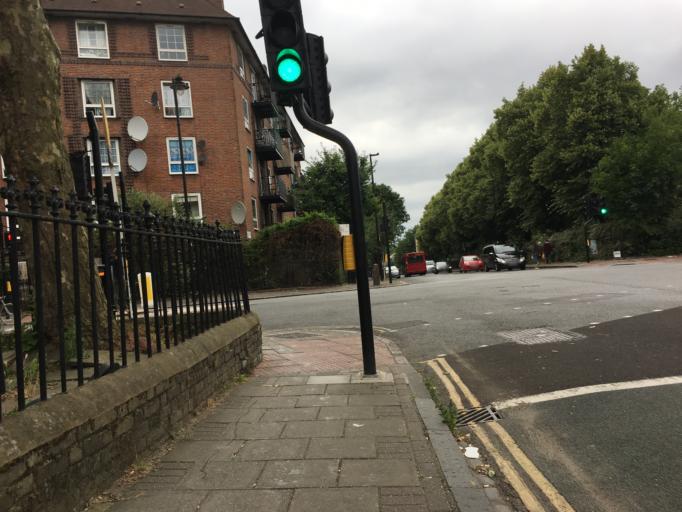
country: GB
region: England
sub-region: Greater London
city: Barnsbury
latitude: 51.5359
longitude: -0.1108
